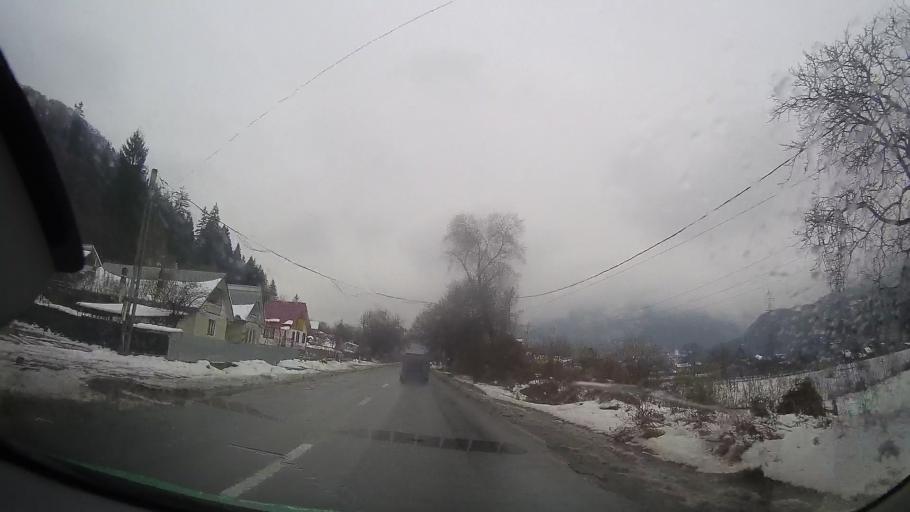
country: RO
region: Neamt
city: Viisoara
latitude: 46.9280
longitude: 26.2345
